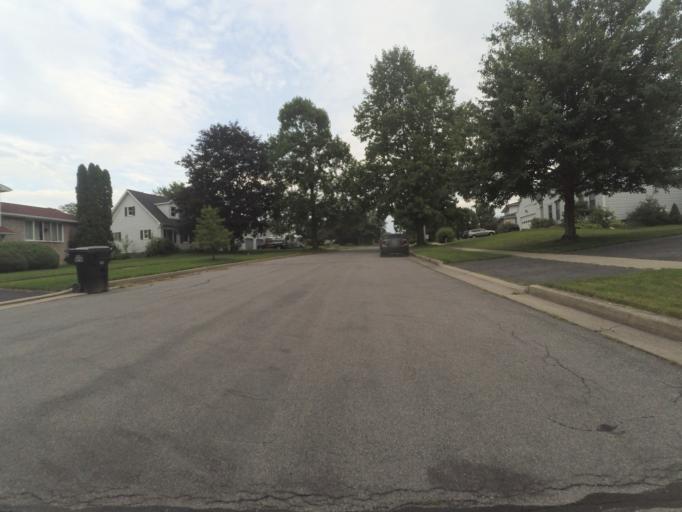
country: US
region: Pennsylvania
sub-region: Centre County
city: State College
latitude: 40.7755
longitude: -77.8666
